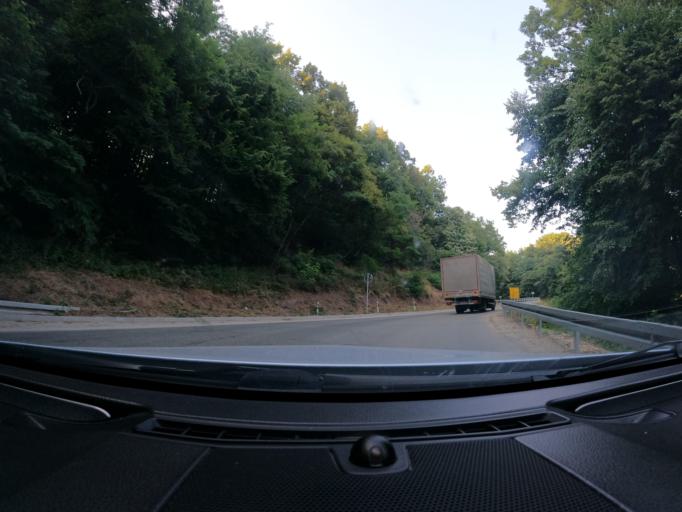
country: RS
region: Autonomna Pokrajina Vojvodina
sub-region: Juznobacki Okrug
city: Beocin
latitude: 45.1512
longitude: 19.7141
